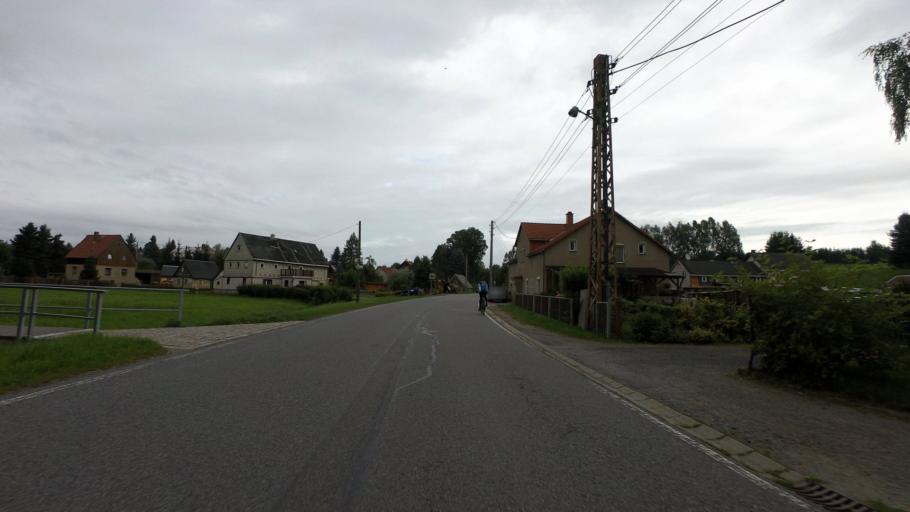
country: DE
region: Saxony
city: Berthelsdorf
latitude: 51.0456
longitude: 14.2223
